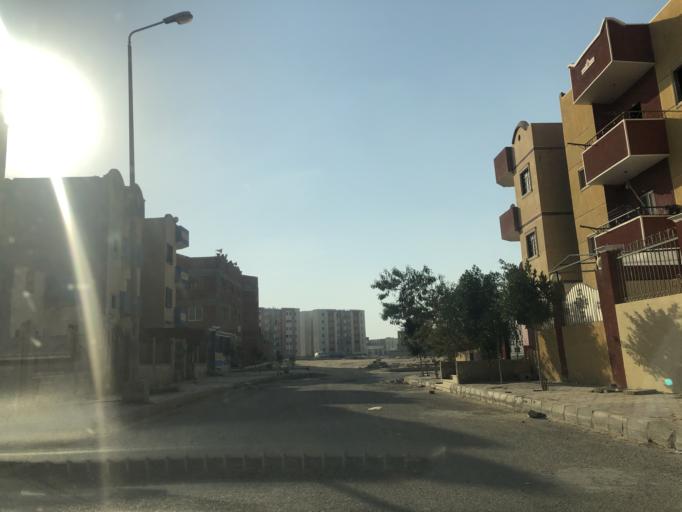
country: EG
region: Al Jizah
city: Madinat Sittah Uktubar
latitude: 29.9065
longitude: 30.9315
